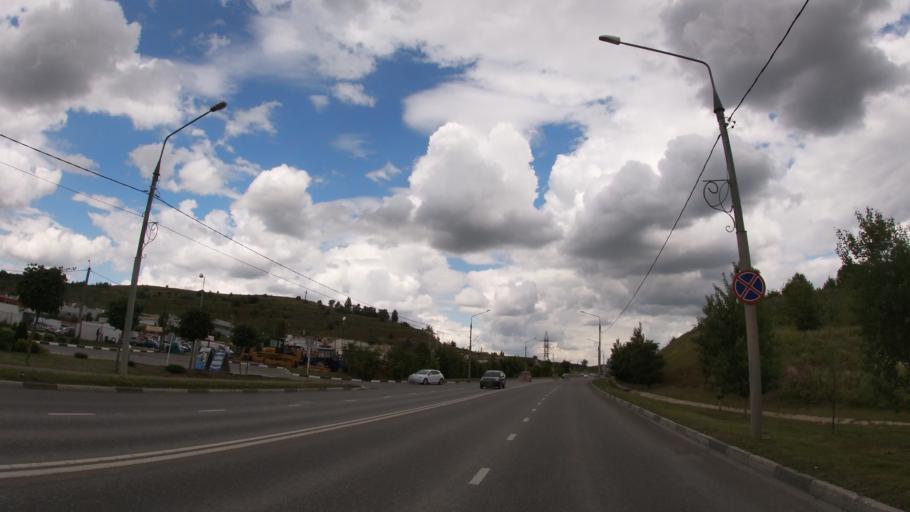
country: RU
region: Belgorod
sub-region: Belgorodskiy Rayon
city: Belgorod
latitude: 50.6149
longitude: 36.6139
